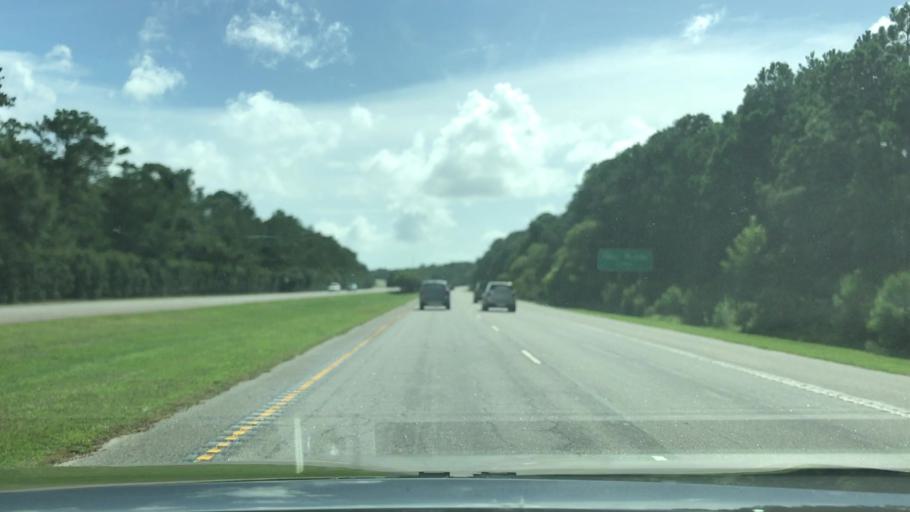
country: US
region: South Carolina
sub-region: Beaufort County
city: Hilton Head Island
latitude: 32.1985
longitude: -80.7574
